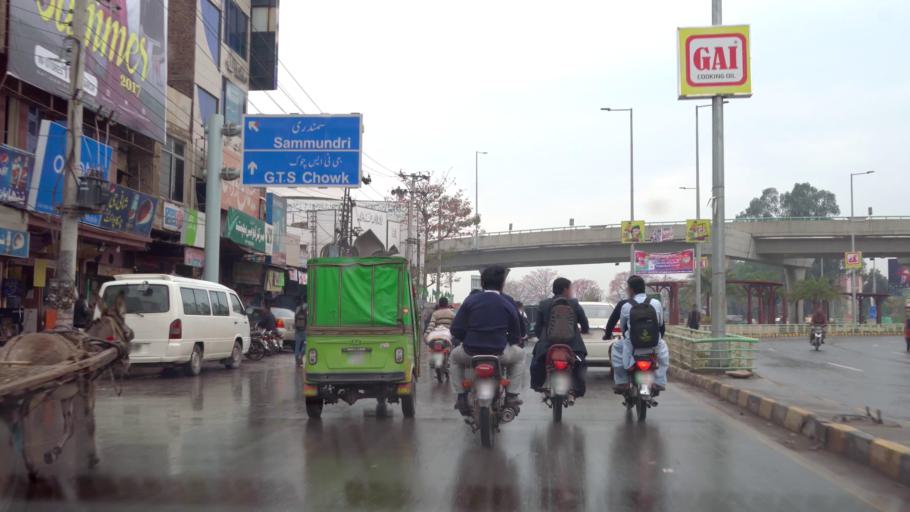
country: PK
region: Punjab
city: Faisalabad
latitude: 31.4090
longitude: 73.0968
